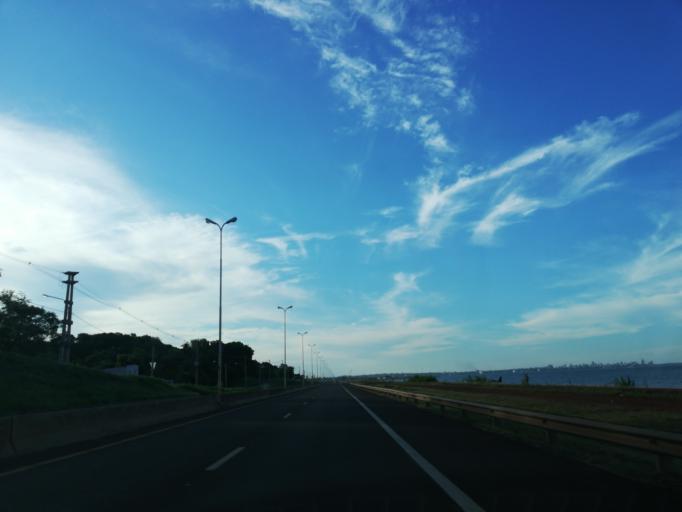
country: AR
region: Misiones
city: Garupa
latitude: -27.4410
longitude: -55.8517
